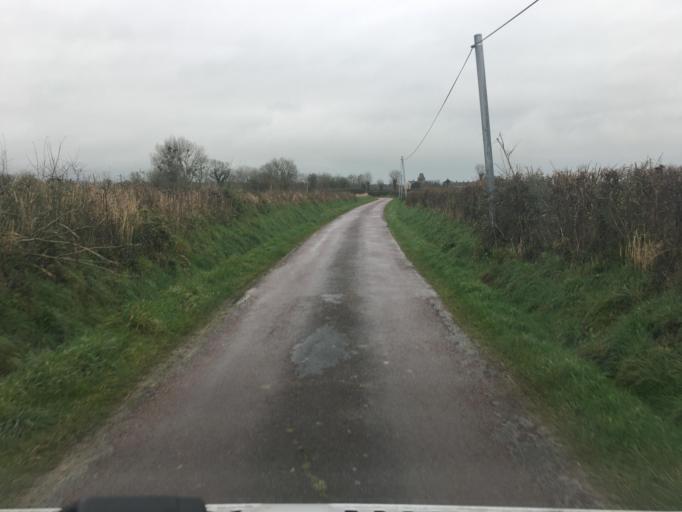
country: FR
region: Lower Normandy
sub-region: Departement de la Manche
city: Sainte-Mere-Eglise
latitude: 49.4319
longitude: -1.2616
